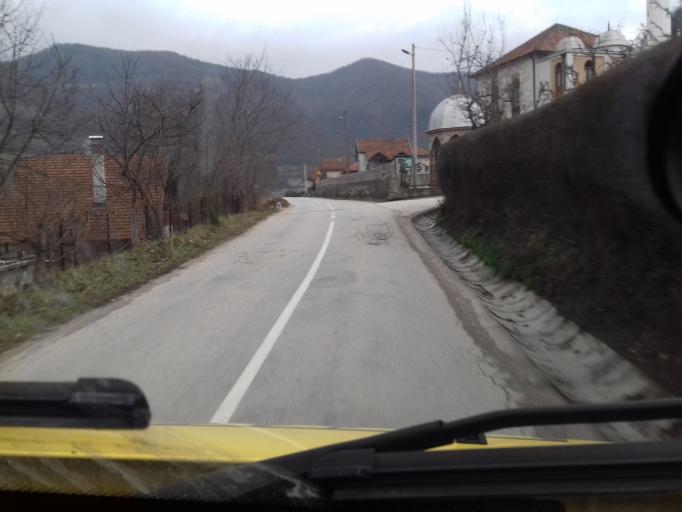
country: BA
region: Federation of Bosnia and Herzegovina
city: Zenica
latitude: 44.1557
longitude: 17.9620
